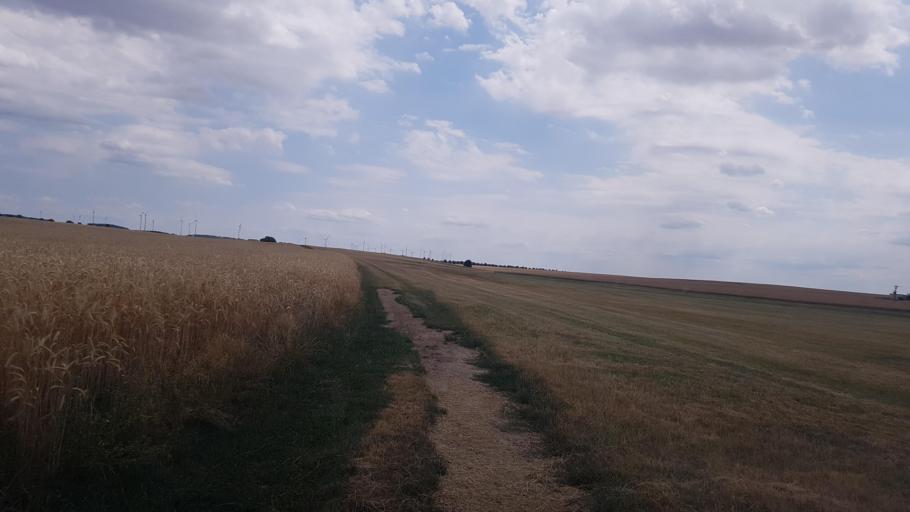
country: DE
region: Brandenburg
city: Juterbog
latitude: 51.9653
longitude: 13.0645
